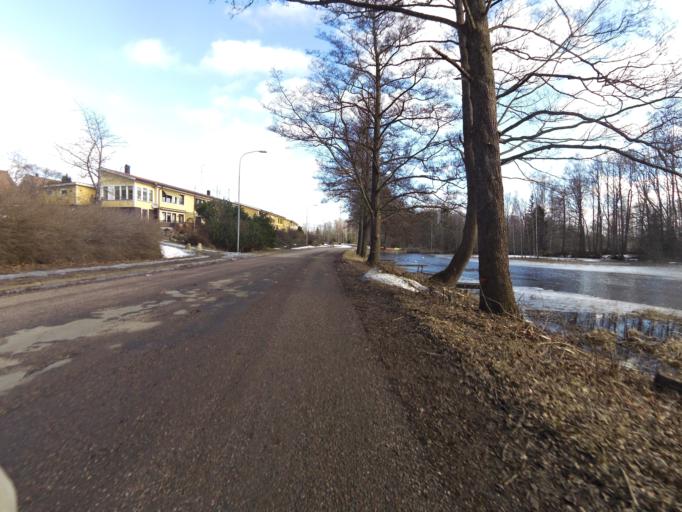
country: SE
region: Uppsala
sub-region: Alvkarleby Kommun
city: Skutskaer
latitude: 60.6489
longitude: 17.3701
